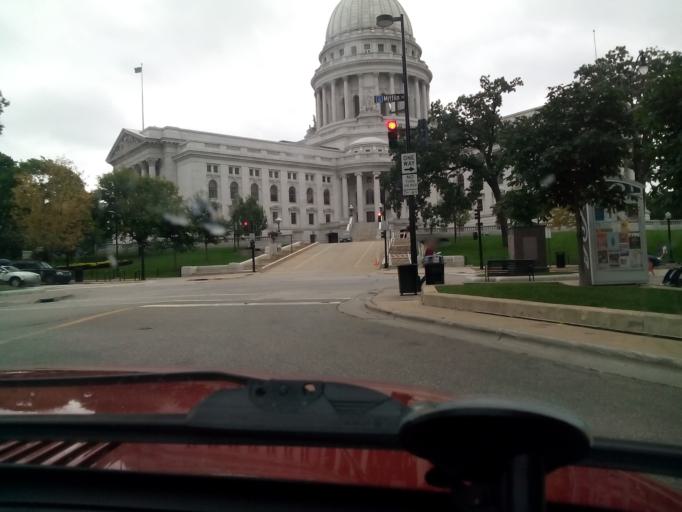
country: US
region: Wisconsin
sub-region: Dane County
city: Madison
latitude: 43.0757
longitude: -89.3856
